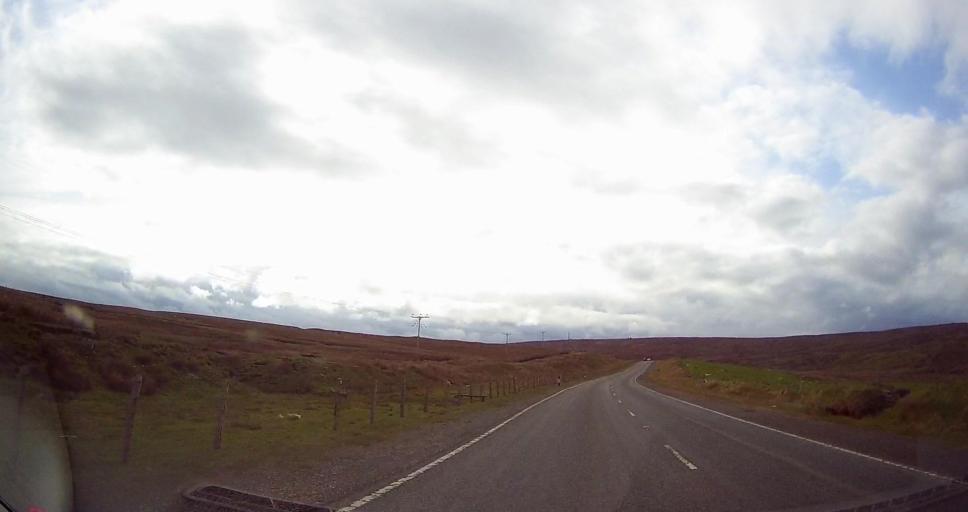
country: GB
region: Scotland
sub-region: Shetland Islands
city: Lerwick
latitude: 60.4438
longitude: -1.2376
